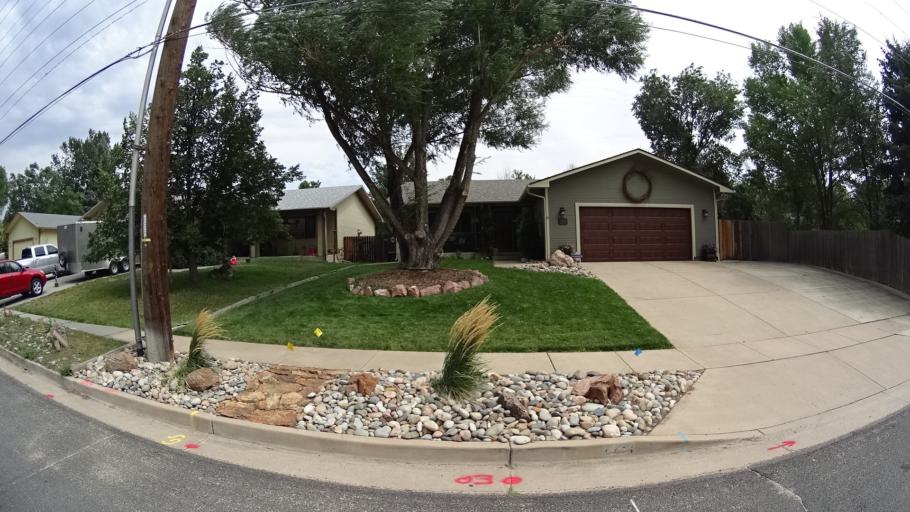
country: US
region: Colorado
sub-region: El Paso County
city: Colorado Springs
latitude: 38.8927
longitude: -104.8126
